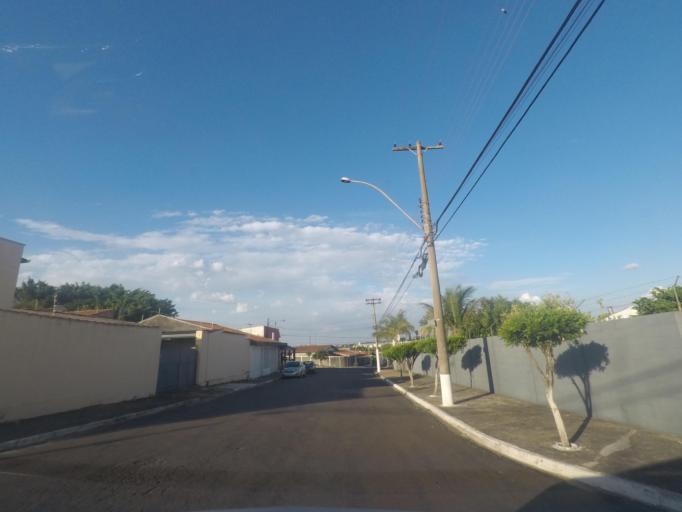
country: BR
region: Sao Paulo
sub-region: Sumare
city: Sumare
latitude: -22.8152
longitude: -47.2836
